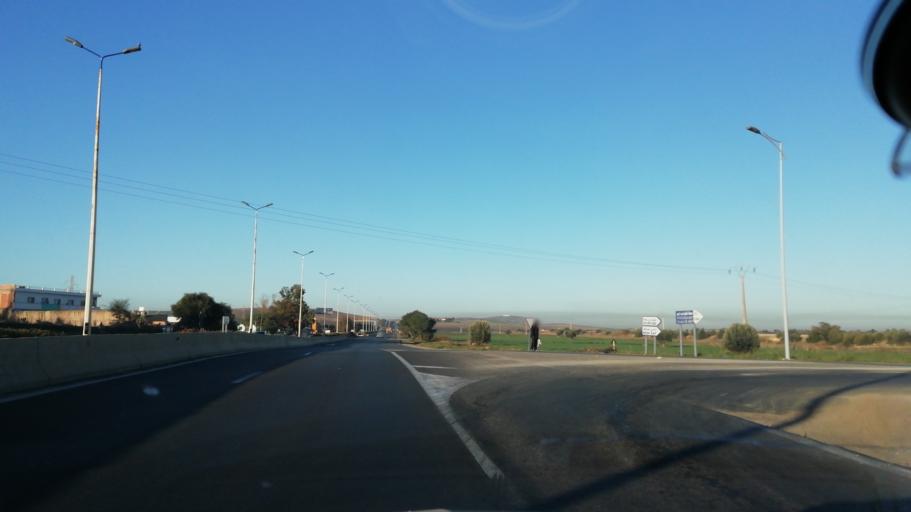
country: DZ
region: Ain Temouchent
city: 'Ain Temouchent
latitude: 35.2954
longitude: -1.1843
